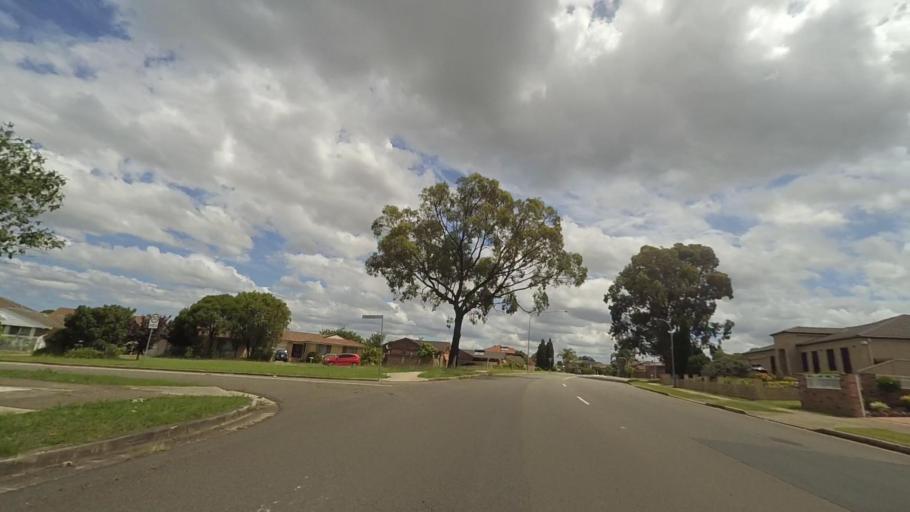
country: AU
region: New South Wales
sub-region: Fairfield
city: Cabramatta West
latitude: -33.8733
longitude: 150.9099
